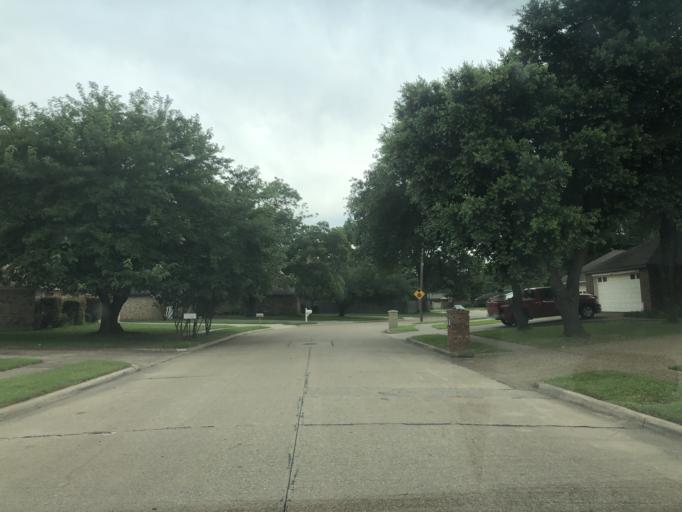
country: US
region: Texas
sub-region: Dallas County
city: Irving
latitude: 32.7859
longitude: -96.9750
